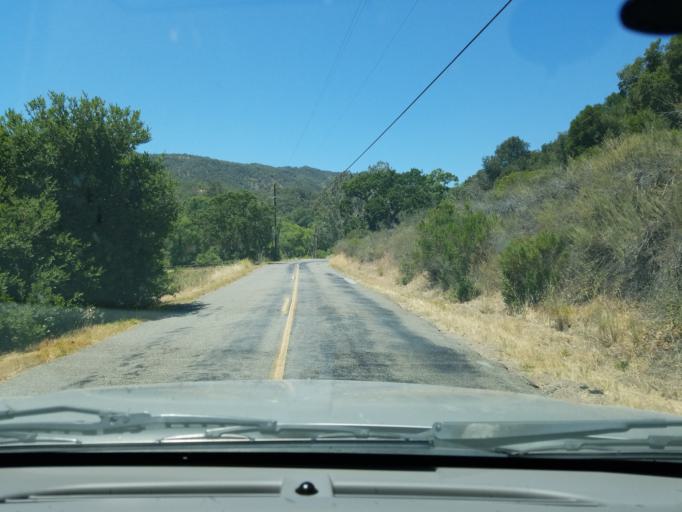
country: US
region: California
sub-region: Monterey County
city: Carmel Valley Village
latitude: 36.4437
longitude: -121.6647
